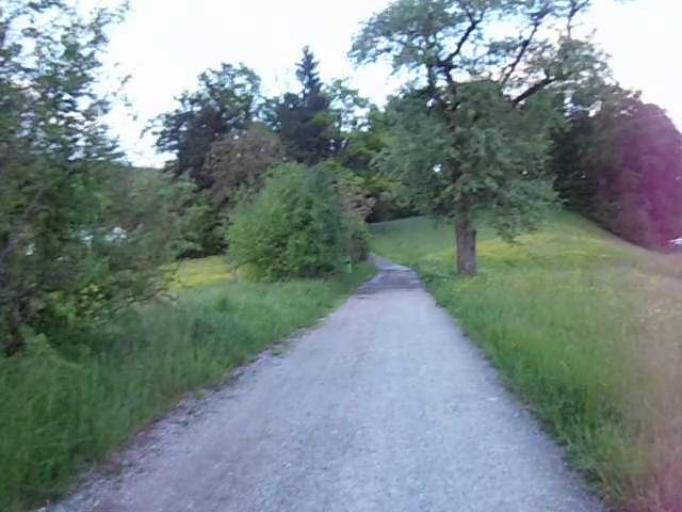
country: CH
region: Zurich
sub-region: Bezirk Hinwil
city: Rueti / Oberdorf
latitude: 47.2525
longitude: 8.8656
